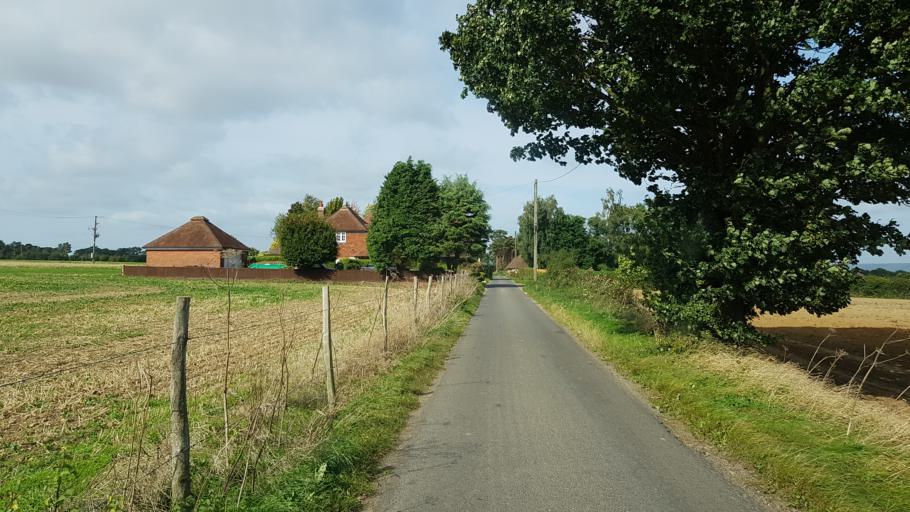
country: GB
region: England
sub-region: Kent
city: Harrietsham
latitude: 51.2382
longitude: 0.6233
